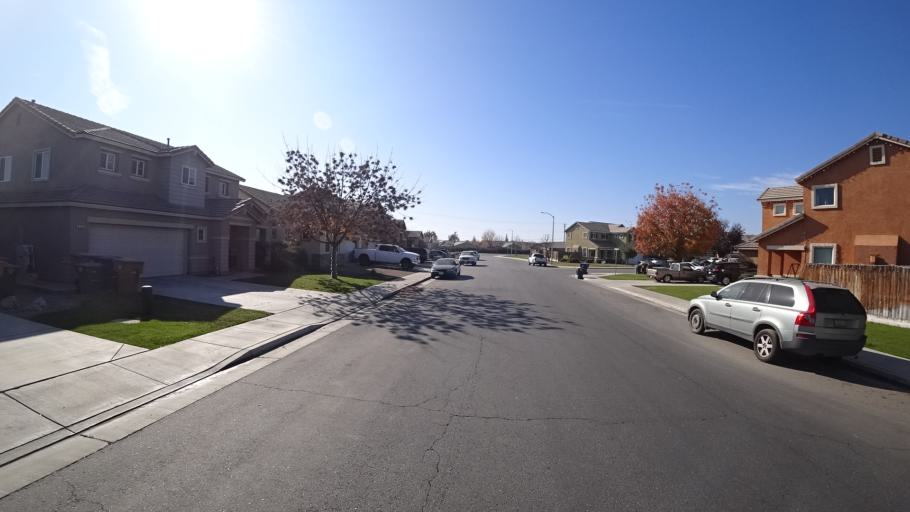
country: US
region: California
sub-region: Kern County
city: Greenfield
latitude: 35.2753
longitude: -119.0627
